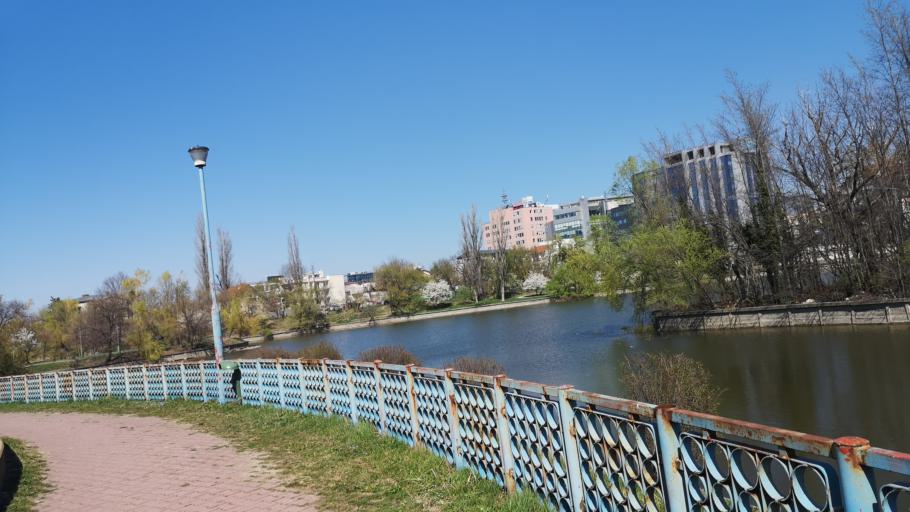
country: RO
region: Ilfov
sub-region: Comuna Otopeni
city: Otopeni
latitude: 44.4887
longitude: 26.0768
